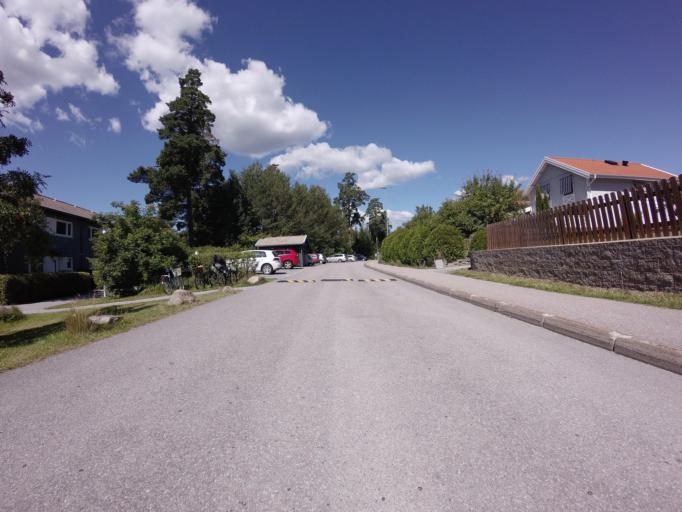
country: SE
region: Stockholm
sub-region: Jarfalla Kommun
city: Jakobsberg
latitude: 59.4564
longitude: 17.8885
